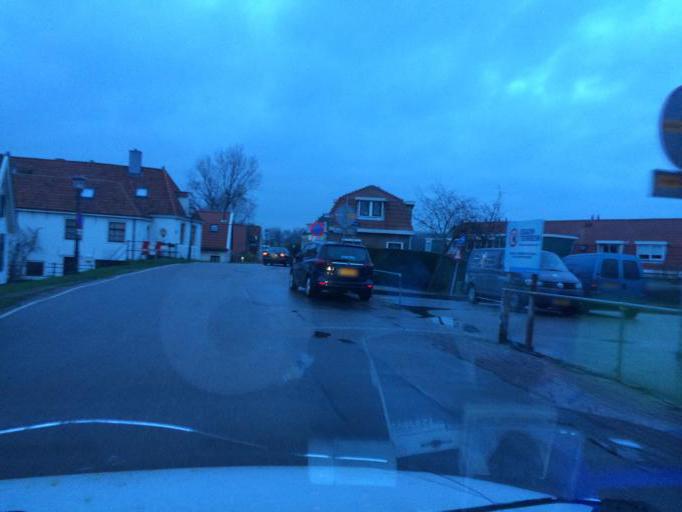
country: NL
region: North Holland
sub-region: Gemeente Velsen
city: Velsen-Zuid
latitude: 52.4156
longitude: 4.6766
